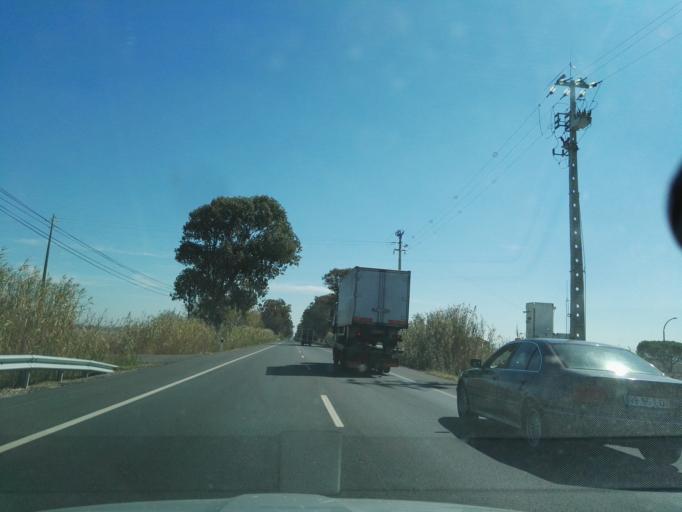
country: PT
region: Santarem
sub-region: Benavente
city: Samora Correia
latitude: 38.9366
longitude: -8.9282
